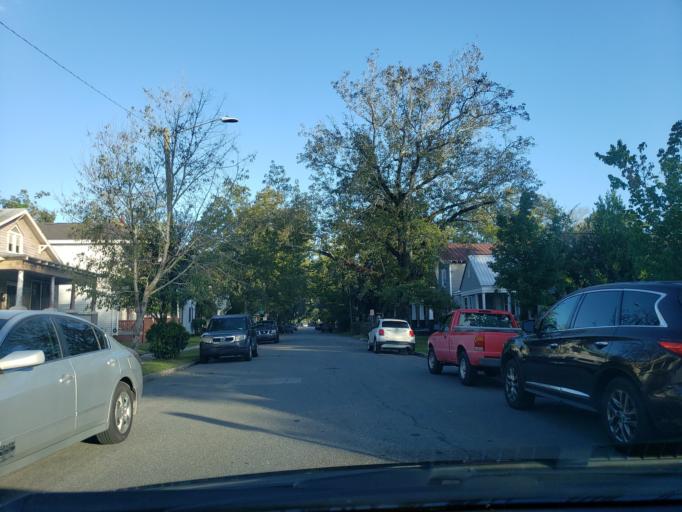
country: US
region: Georgia
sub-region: Chatham County
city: Savannah
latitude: 32.0554
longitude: -81.0890
